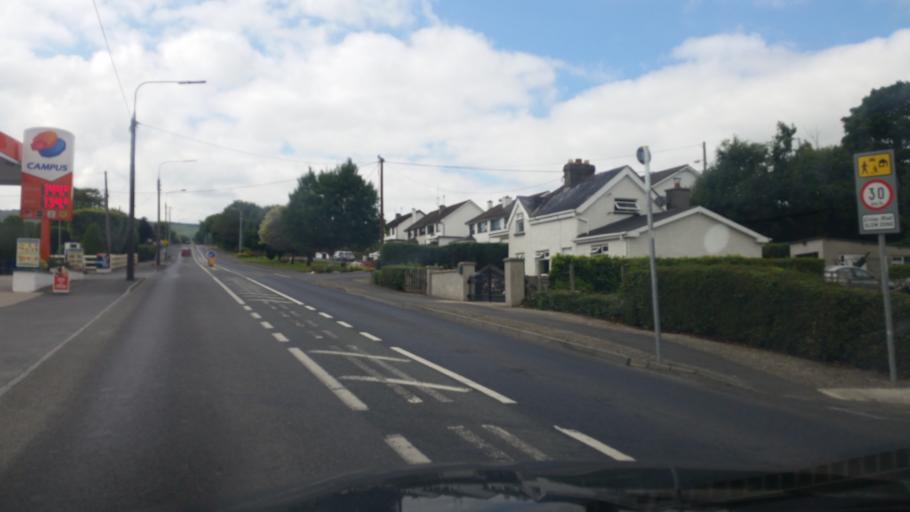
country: IE
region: Leinster
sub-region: Loch Garman
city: Bunclody
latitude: 52.6570
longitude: -6.6626
